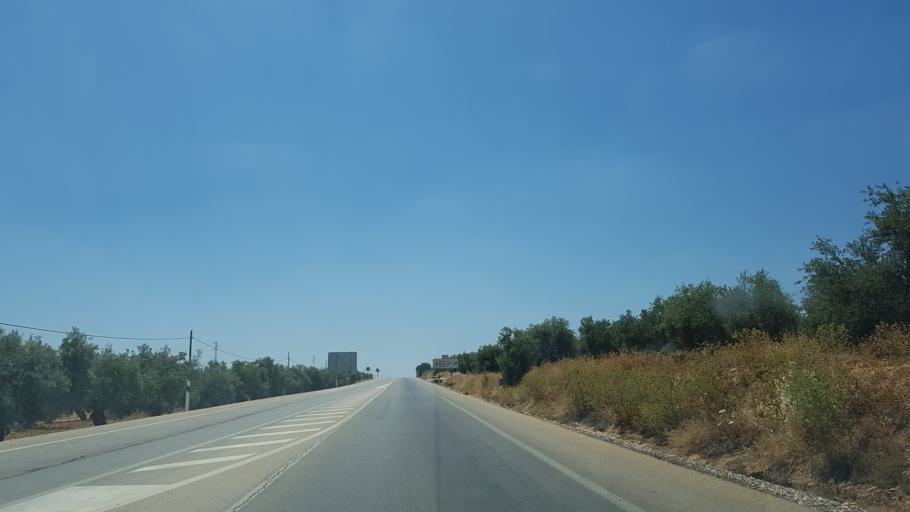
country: ES
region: Andalusia
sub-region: Provincia de Sevilla
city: Herrera
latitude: 37.3674
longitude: -4.8123
